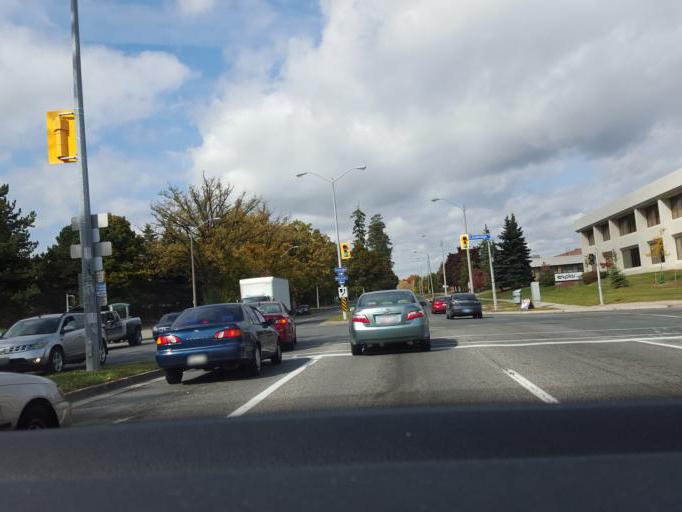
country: CA
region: Ontario
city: Scarborough
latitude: 43.8087
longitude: -79.2026
